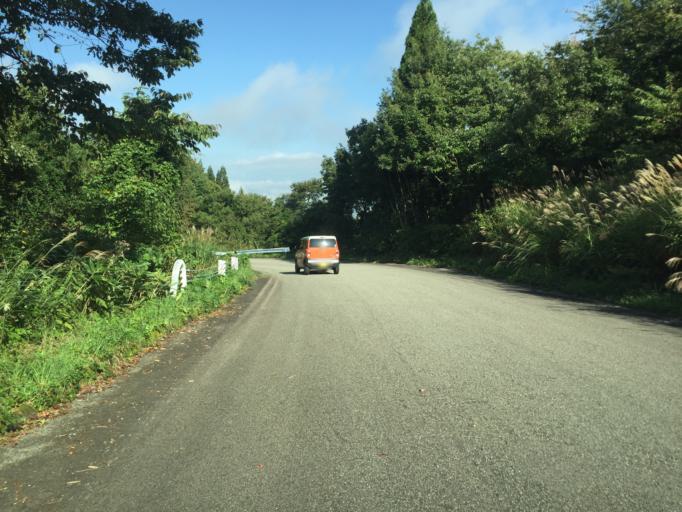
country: JP
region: Fukushima
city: Inawashiro
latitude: 37.4839
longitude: 139.9742
